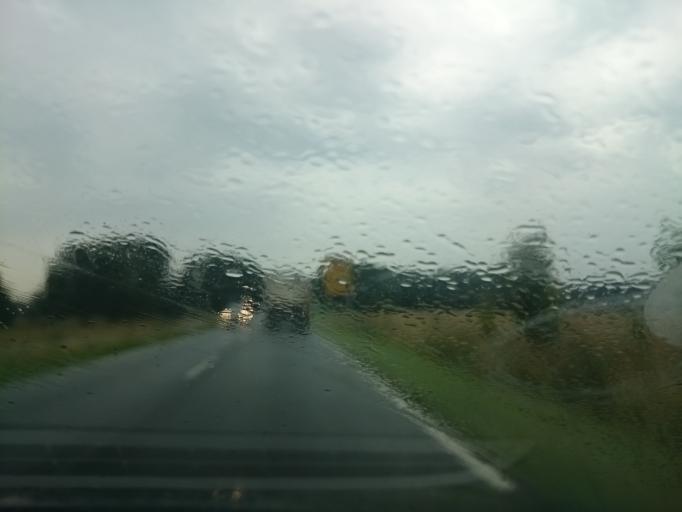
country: DE
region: Brandenburg
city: Gransee
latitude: 52.8713
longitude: 13.1654
